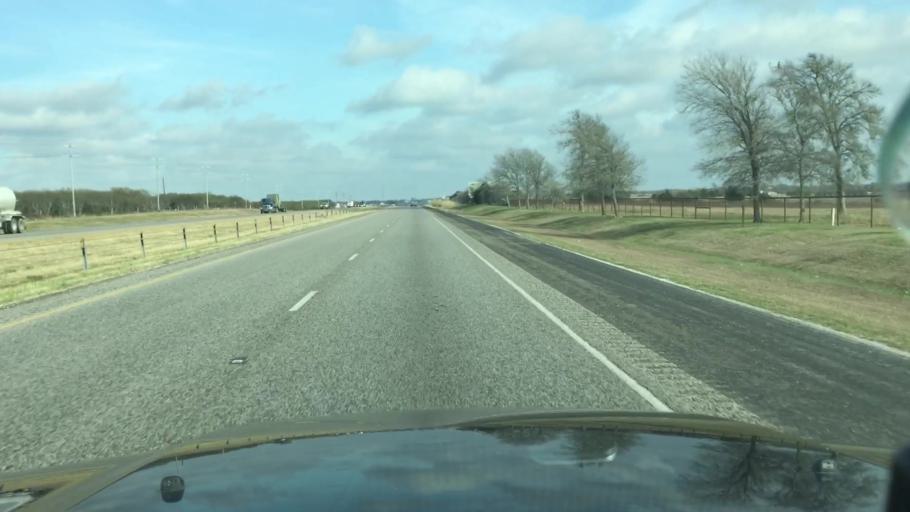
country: US
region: Texas
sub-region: Washington County
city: Brenham
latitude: 30.1377
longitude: -96.3236
